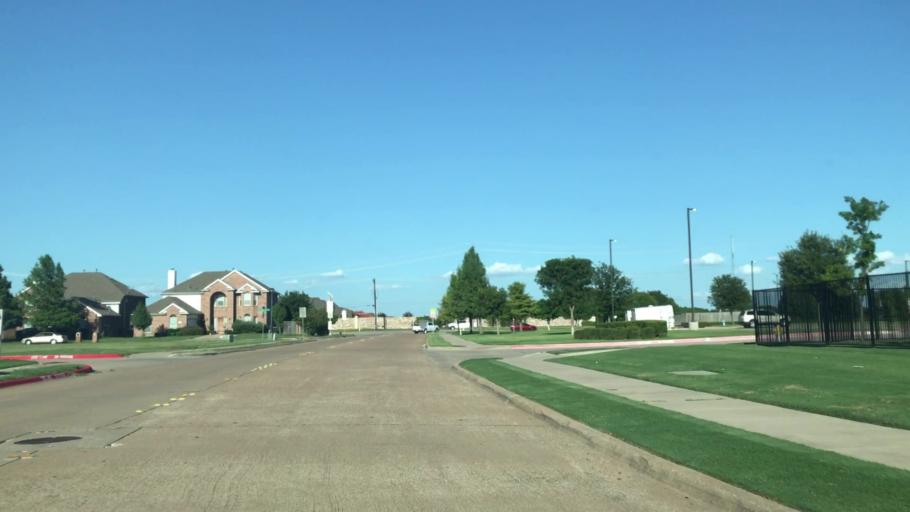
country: US
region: Texas
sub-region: Collin County
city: Frisco
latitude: 33.1236
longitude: -96.7697
